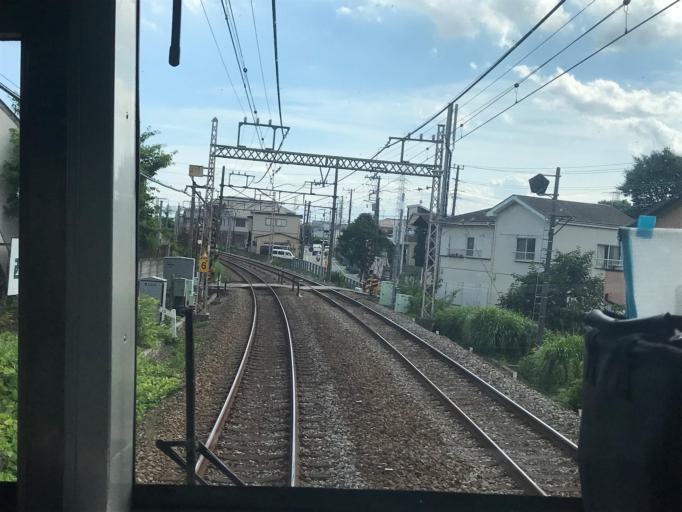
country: JP
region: Kanagawa
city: Atsugi
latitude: 35.4128
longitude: 139.3372
